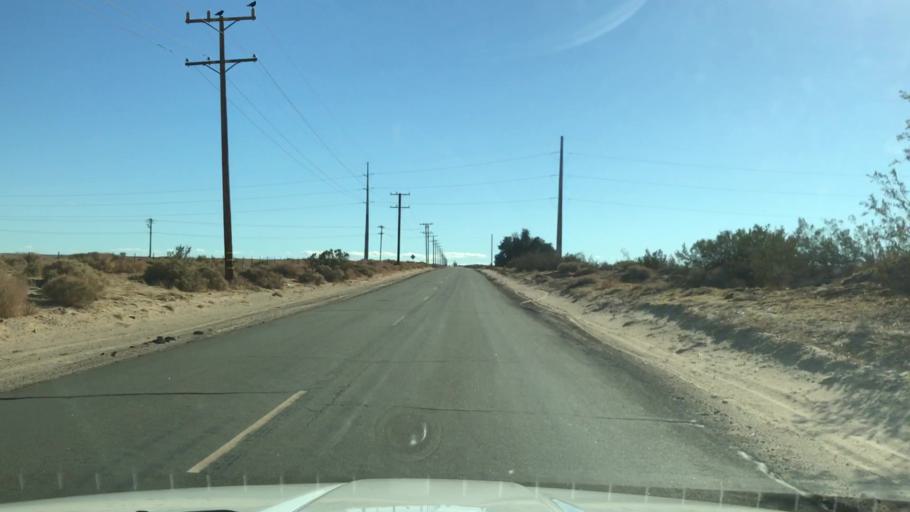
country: US
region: California
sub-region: Kern County
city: California City
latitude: 35.2590
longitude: -117.9859
